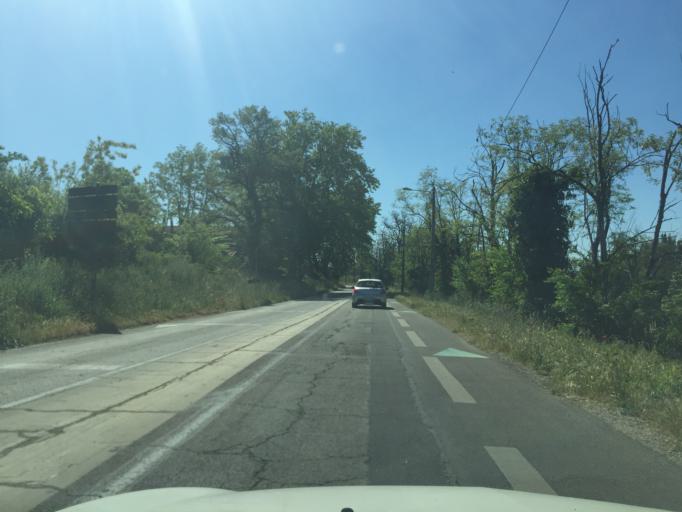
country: FR
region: Provence-Alpes-Cote d'Azur
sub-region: Departement du Vaucluse
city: Montfavet
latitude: 43.9428
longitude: 4.8661
